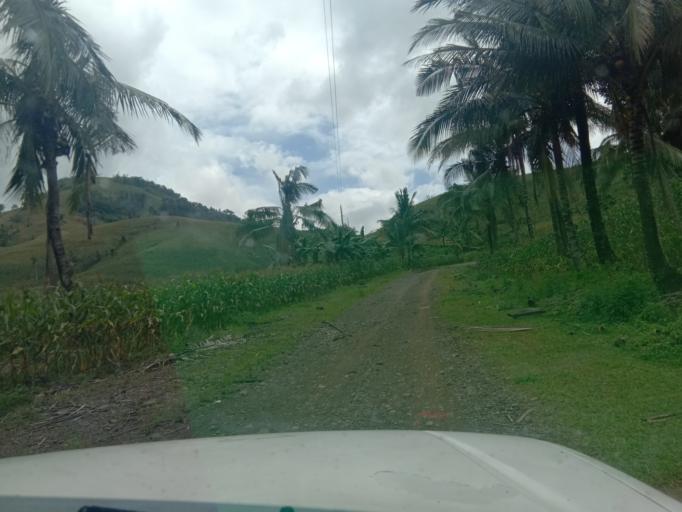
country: PH
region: Western Visayas
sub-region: Province of Capiz
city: Lantangan
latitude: 11.3548
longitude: 122.9154
